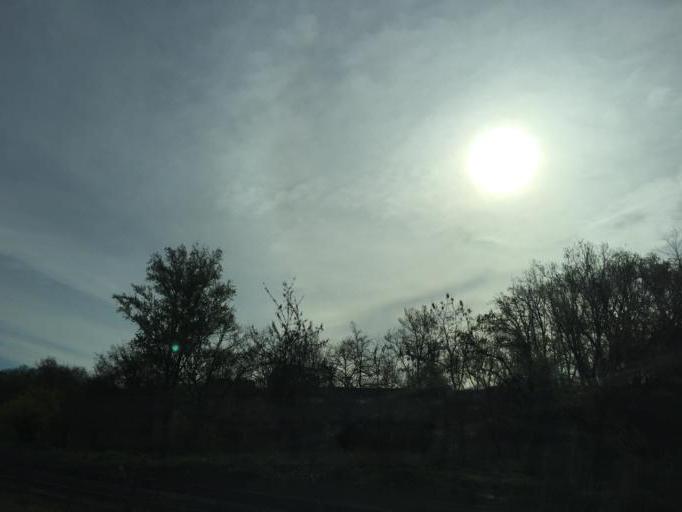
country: FR
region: Midi-Pyrenees
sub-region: Departement de la Haute-Garonne
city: Montastruc-la-Conseillere
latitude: 43.7146
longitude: 1.5962
